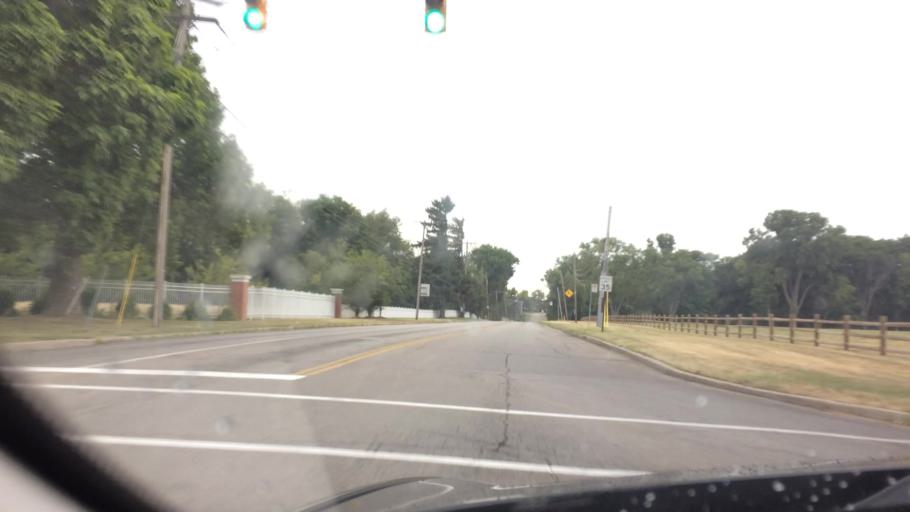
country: US
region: Ohio
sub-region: Lucas County
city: Ottawa Hills
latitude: 41.6528
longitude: -83.6409
